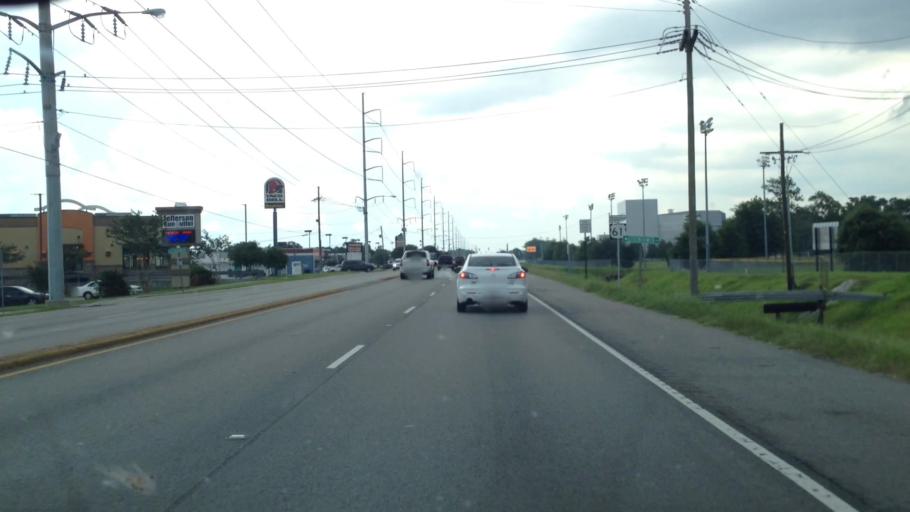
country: US
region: Louisiana
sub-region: Jefferson Parish
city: River Ridge
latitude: 29.9776
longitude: -90.2088
